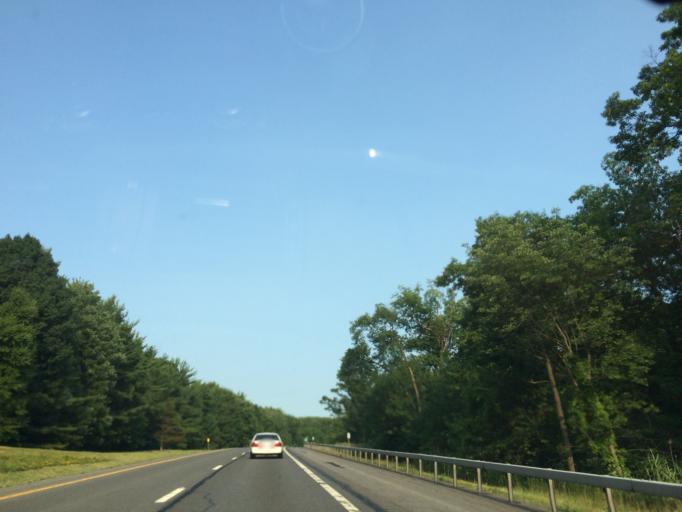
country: US
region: New York
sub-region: Rensselaer County
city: Castleton-on-Hudson
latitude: 42.4929
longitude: -73.7193
